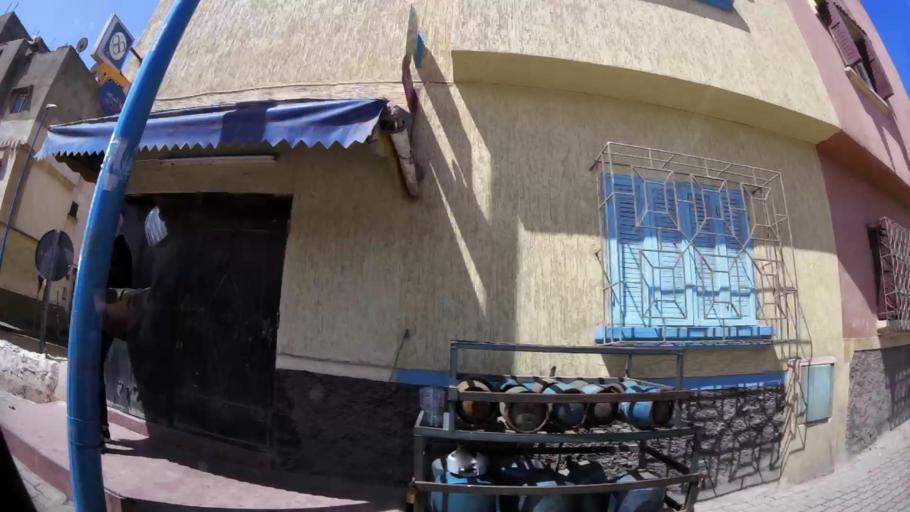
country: MA
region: Grand Casablanca
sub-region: Mohammedia
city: Mohammedia
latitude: 33.6399
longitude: -7.4507
